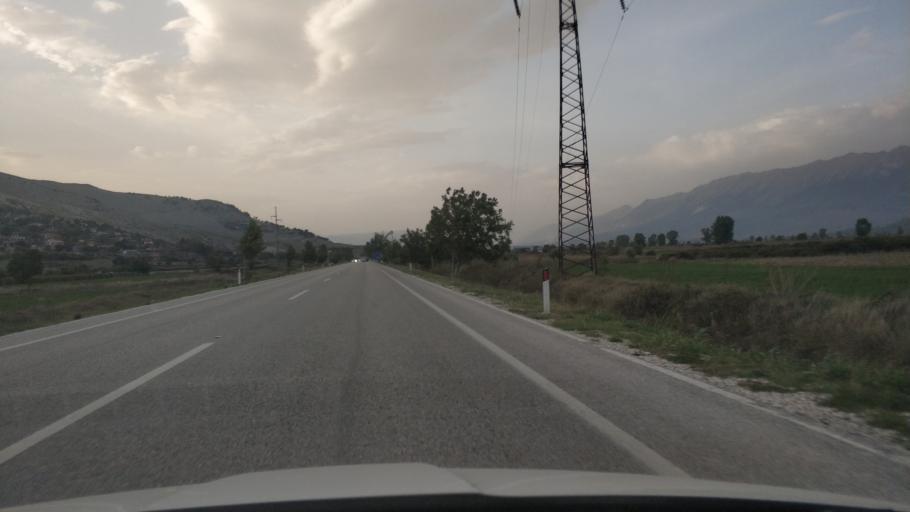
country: AL
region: Gjirokaster
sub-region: Rrethi i Gjirokastres
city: Libohove
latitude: 39.9608
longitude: 20.2453
